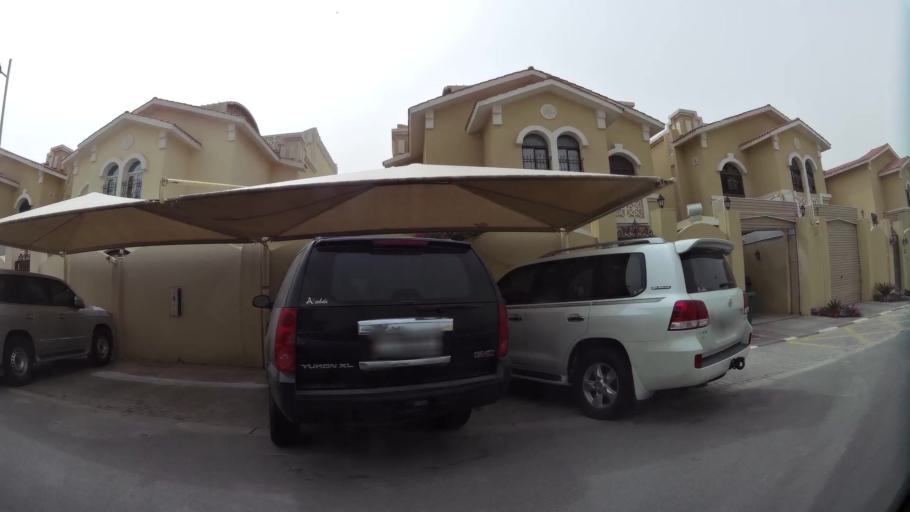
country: QA
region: Baladiyat ad Dawhah
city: Doha
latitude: 25.2286
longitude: 51.5360
